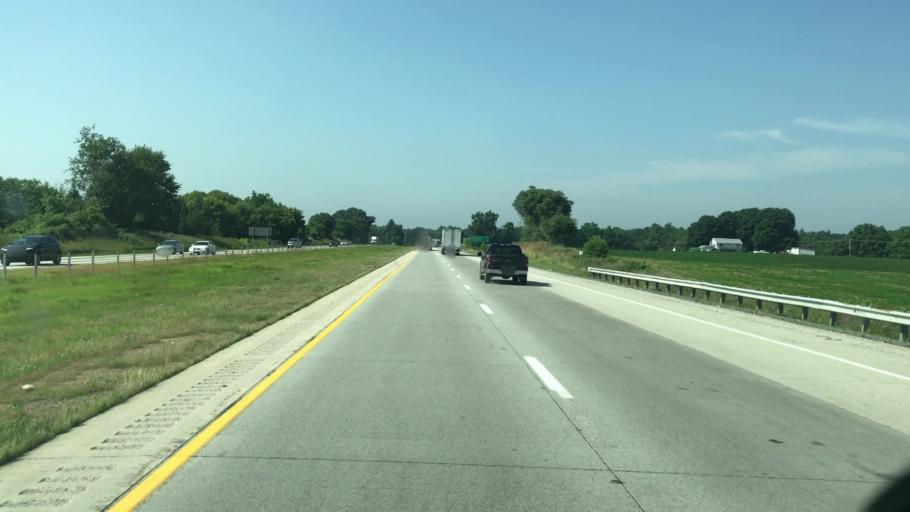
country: US
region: Pennsylvania
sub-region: Franklin County
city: Scotland
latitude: 39.9590
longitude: -77.5802
